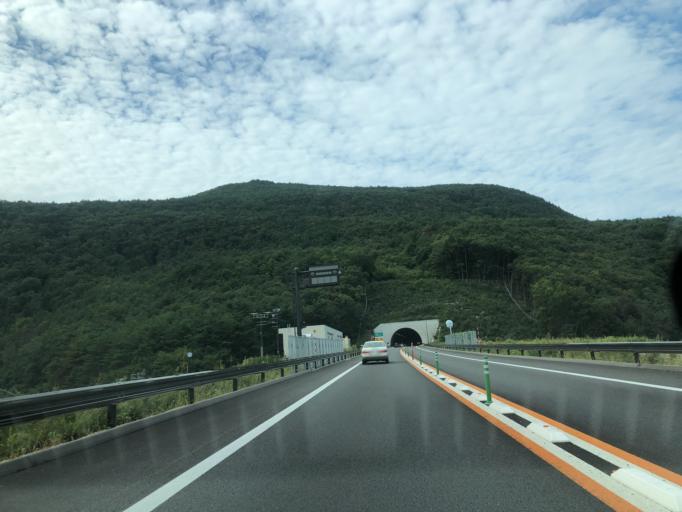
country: JP
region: Fukushima
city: Fukushima-shi
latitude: 37.8072
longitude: 140.4073
